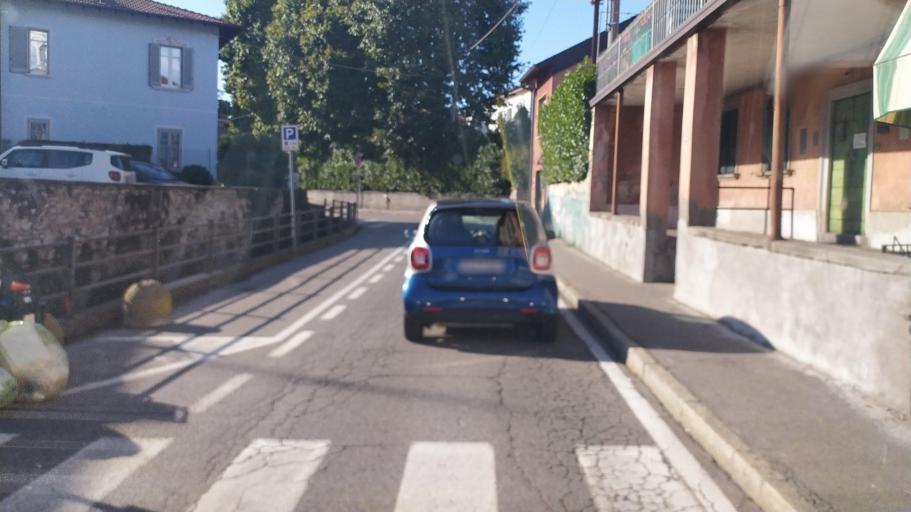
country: IT
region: Lombardy
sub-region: Provincia di Varese
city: Travedona Monate
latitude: 45.8048
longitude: 8.6721
